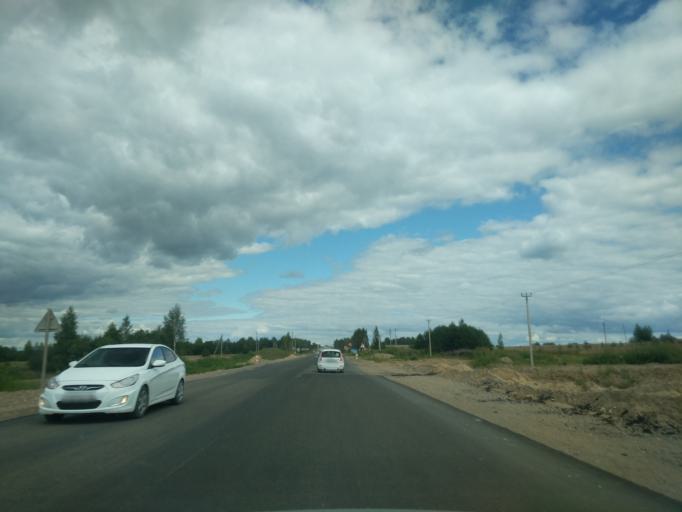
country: RU
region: Kostroma
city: Sudislavl'
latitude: 57.8649
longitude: 41.6275
